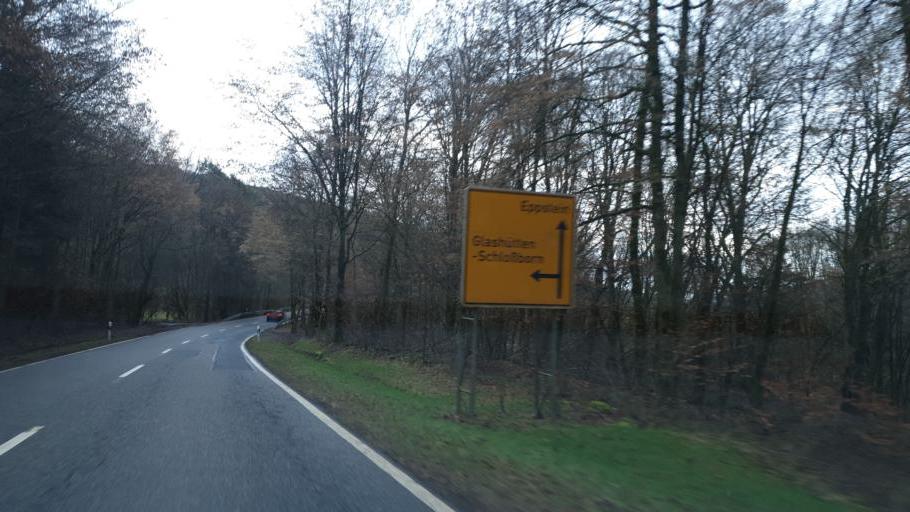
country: DE
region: Hesse
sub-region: Regierungsbezirk Darmstadt
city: Glashutten
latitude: 50.1865
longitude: 8.3600
